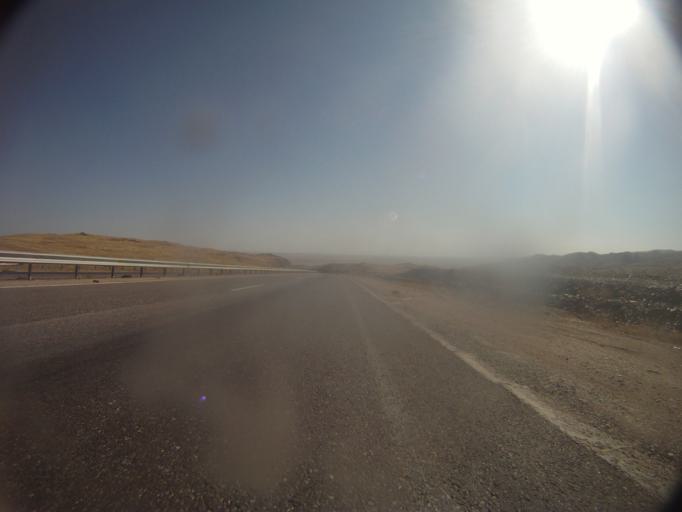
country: KZ
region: Zhambyl
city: Taraz
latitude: 42.7390
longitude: 70.9480
